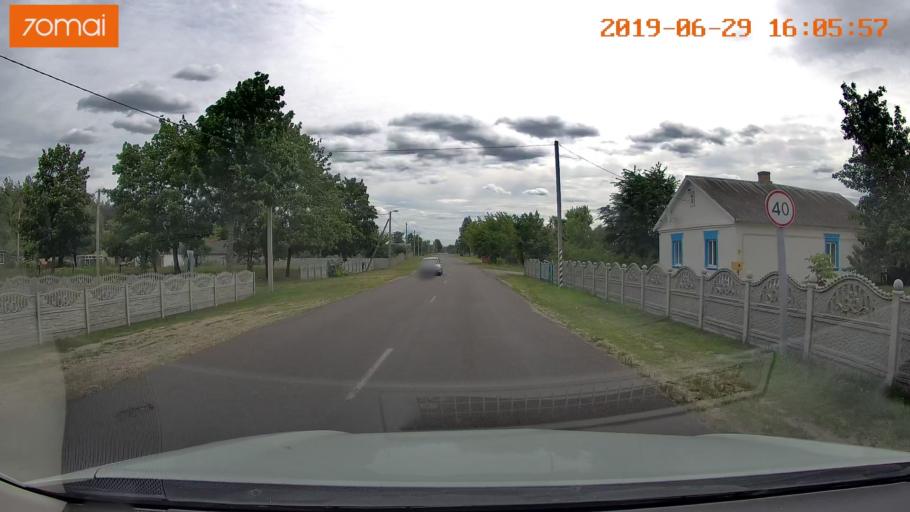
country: BY
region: Brest
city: Luninyets
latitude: 52.2126
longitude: 27.0160
